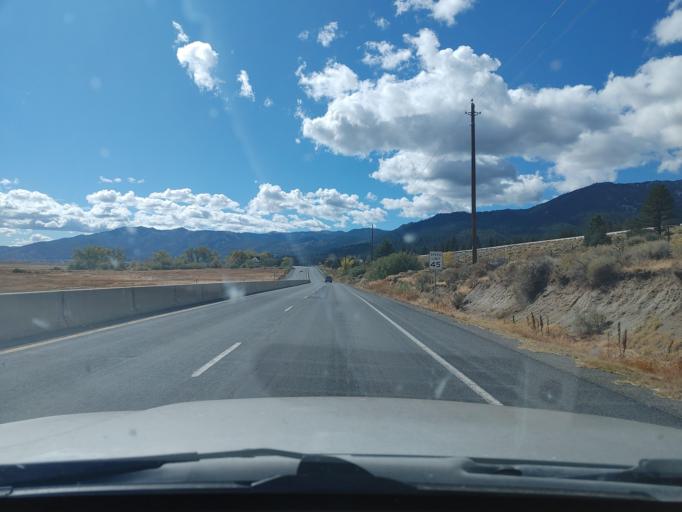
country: US
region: Nevada
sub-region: Carson City
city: Carson City
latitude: 39.3169
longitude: -119.8200
